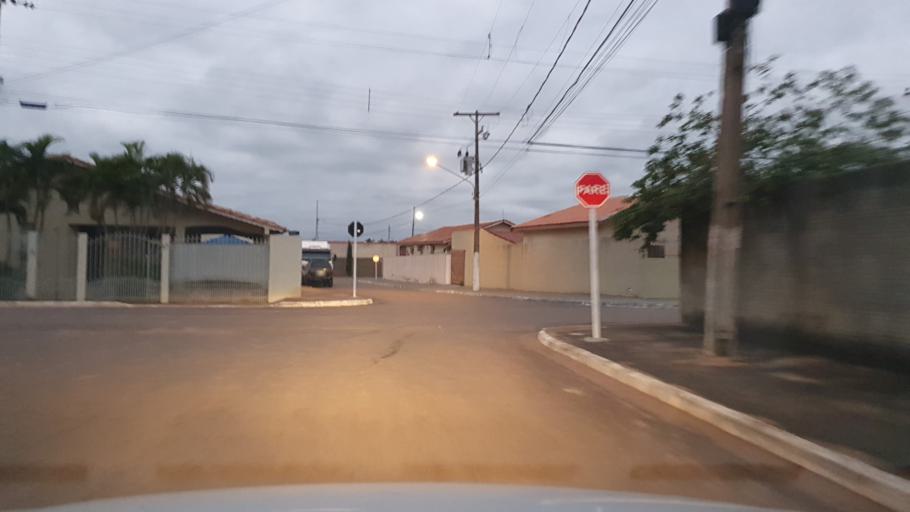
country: BR
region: Mato Grosso
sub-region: Pontes E Lacerda
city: Pontes e Lacerda
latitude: -15.2329
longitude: -59.3161
